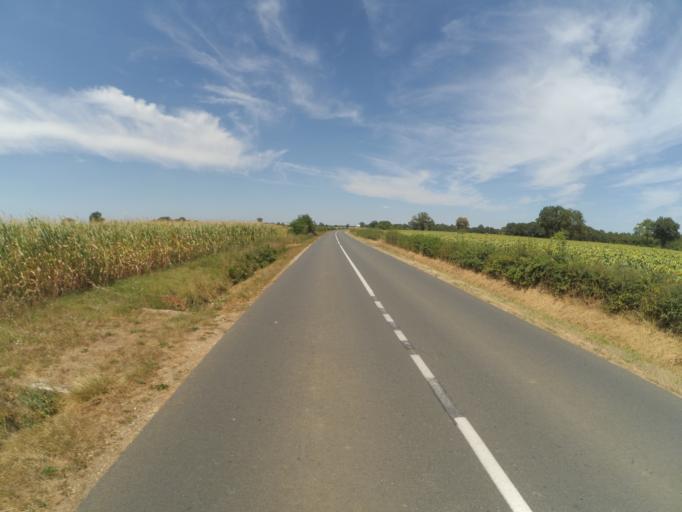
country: FR
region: Poitou-Charentes
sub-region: Departement de la Vienne
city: Availles-Limouzine
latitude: 46.1227
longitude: 0.5606
